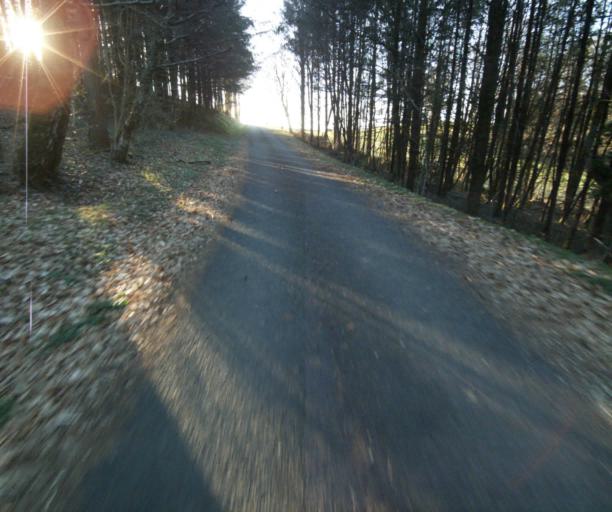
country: FR
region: Limousin
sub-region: Departement de la Correze
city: Saint-Clement
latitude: 45.3579
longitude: 1.6909
